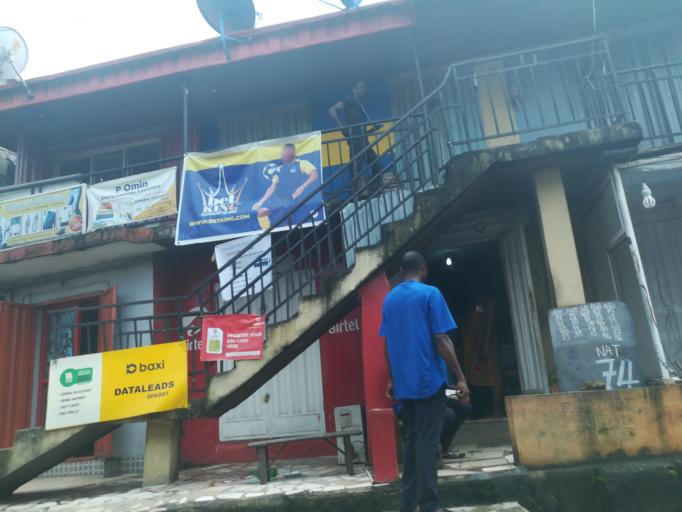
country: NG
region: Lagos
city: Ikeja
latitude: 6.6142
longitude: 3.3488
